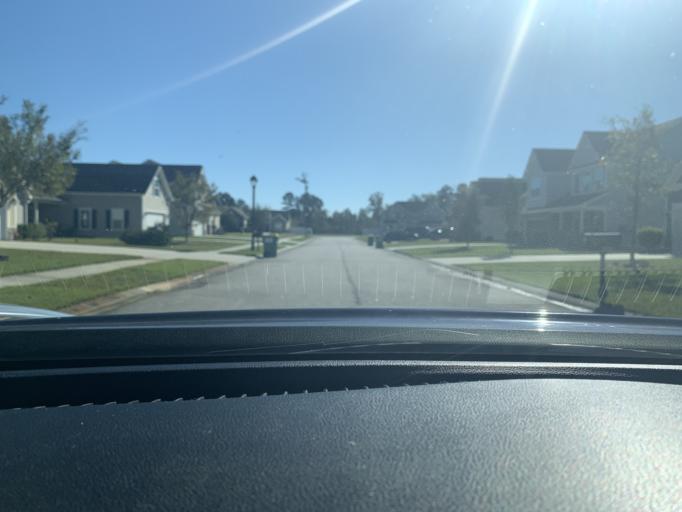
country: US
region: Georgia
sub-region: Chatham County
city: Pooler
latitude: 32.0714
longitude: -81.2697
